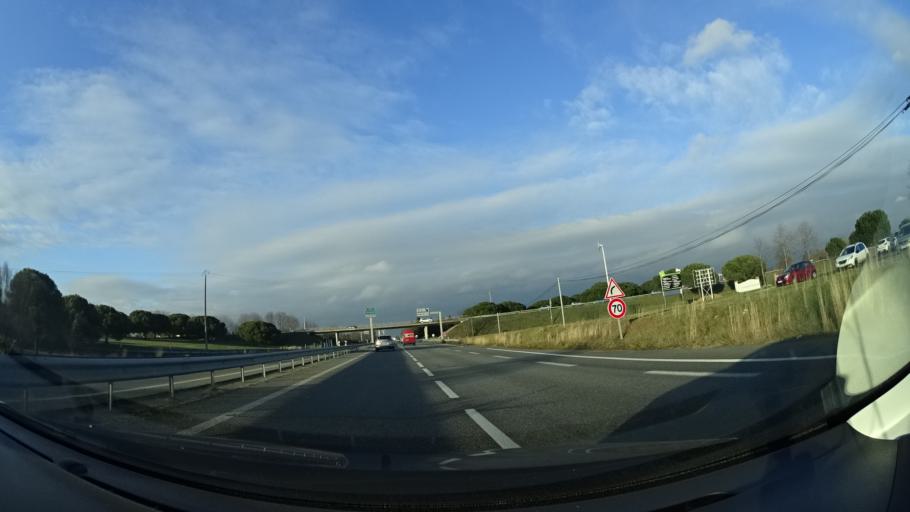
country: FR
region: Midi-Pyrenees
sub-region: Departement de l'Ariege
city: Saint-Jean-du-Falga
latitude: 43.1004
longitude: 1.6330
